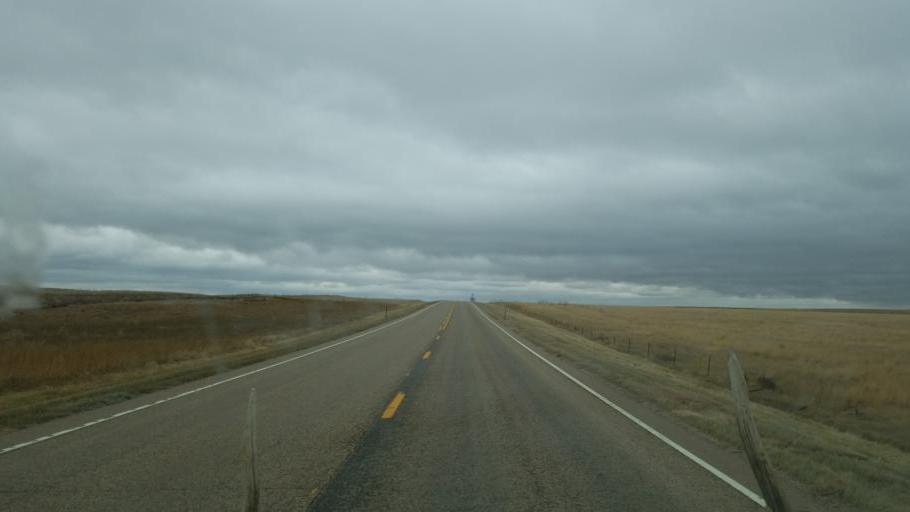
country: US
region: Colorado
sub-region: Cheyenne County
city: Cheyenne Wells
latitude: 38.8151
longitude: -102.5595
